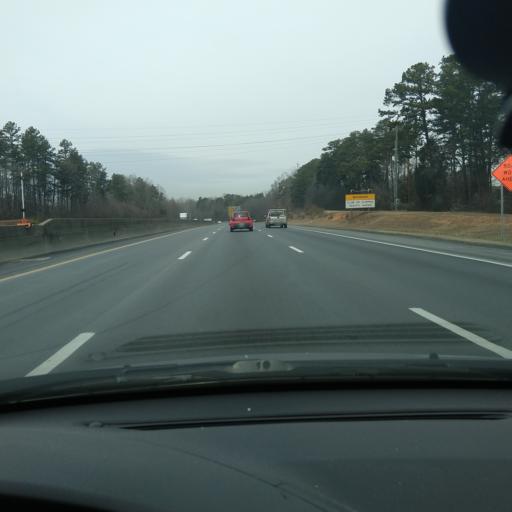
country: US
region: North Carolina
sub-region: Gaston County
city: Gastonia
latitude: 35.2800
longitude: -81.1677
